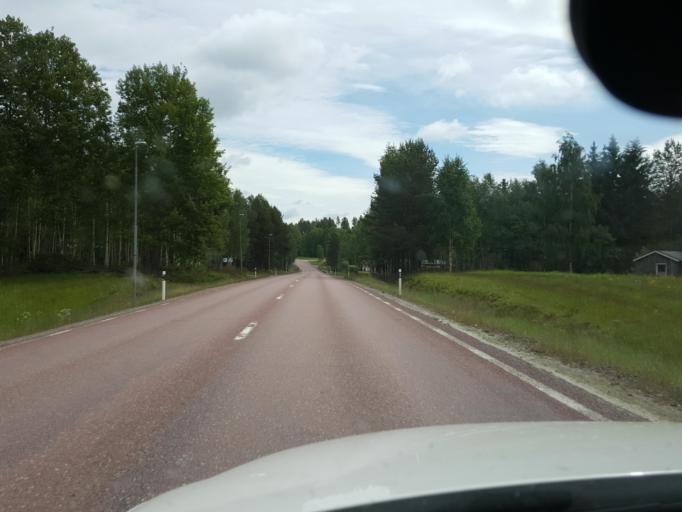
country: SE
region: Gaevleborg
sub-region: Ljusdals Kommun
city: Farila
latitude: 61.8016
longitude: 15.7934
